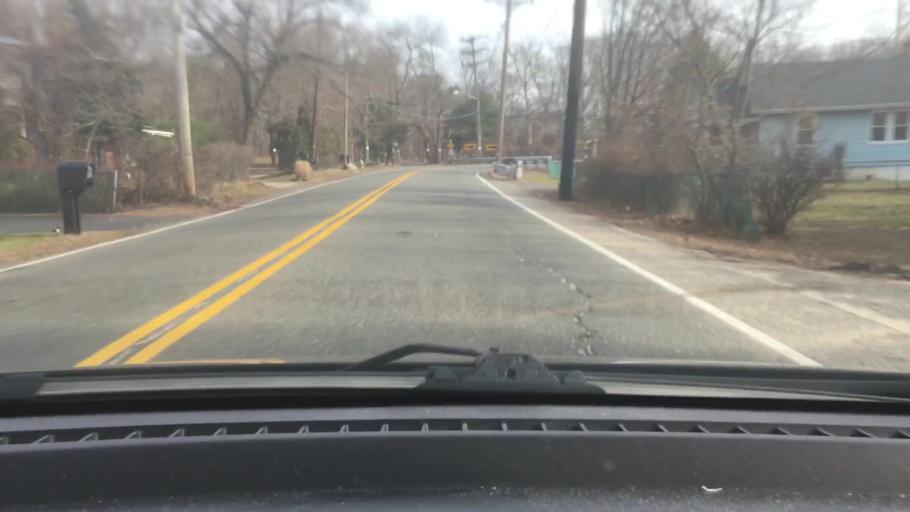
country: US
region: New Jersey
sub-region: Monmouth County
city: Shark River Hills
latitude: 40.2218
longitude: -74.0581
